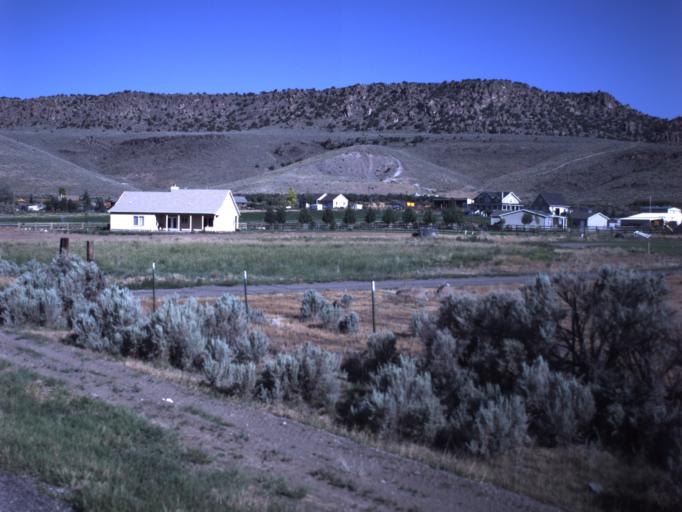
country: US
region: Utah
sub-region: Wayne County
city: Loa
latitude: 38.4623
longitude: -111.6031
